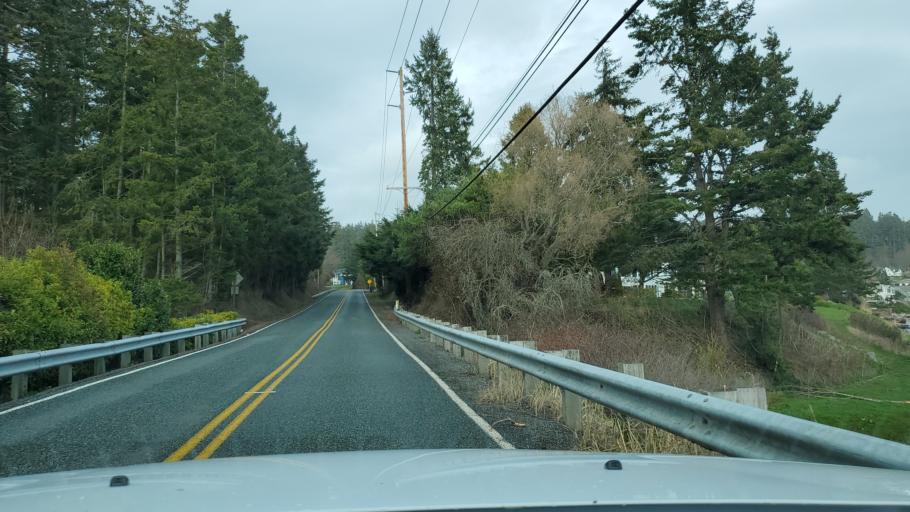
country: US
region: Washington
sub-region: Skagit County
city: Anacortes
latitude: 48.4237
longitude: -122.6096
